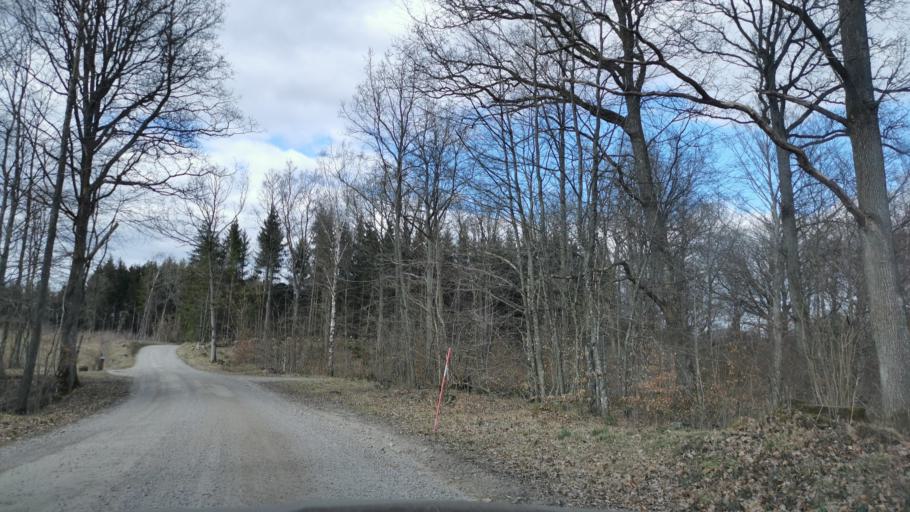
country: SE
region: Skane
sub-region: Sjobo Kommun
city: Sjoebo
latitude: 55.7453
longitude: 13.8379
